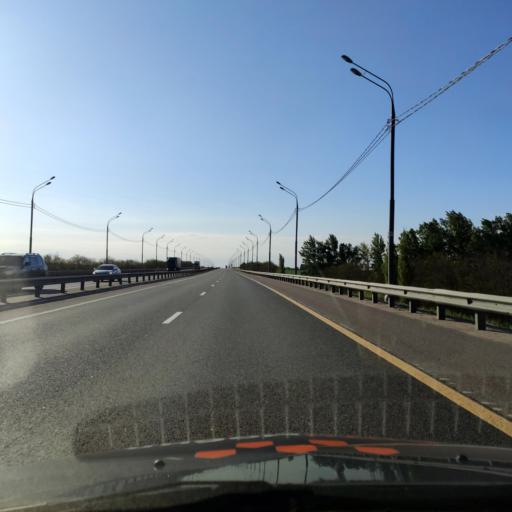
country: RU
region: Lipetsk
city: Khlevnoye
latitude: 52.2376
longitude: 39.0744
